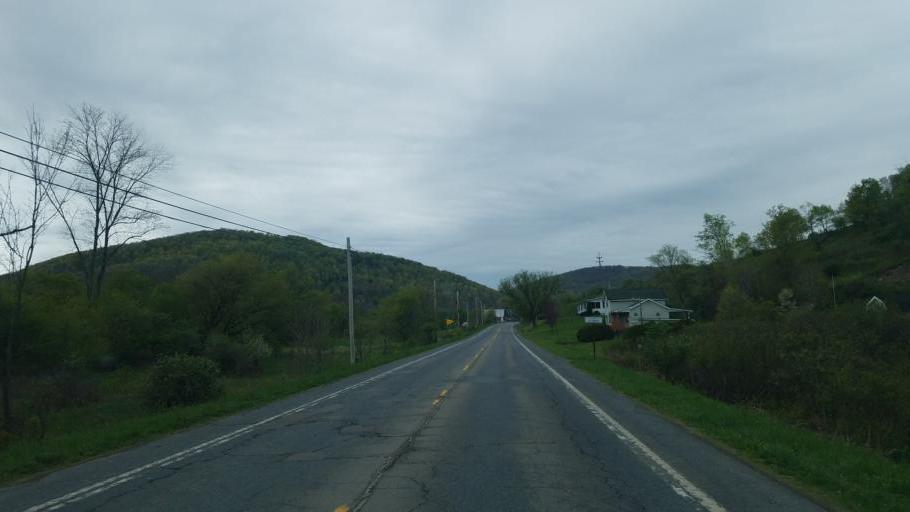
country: US
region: Pennsylvania
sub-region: Tioga County
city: Westfield
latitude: 41.9166
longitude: -77.6163
